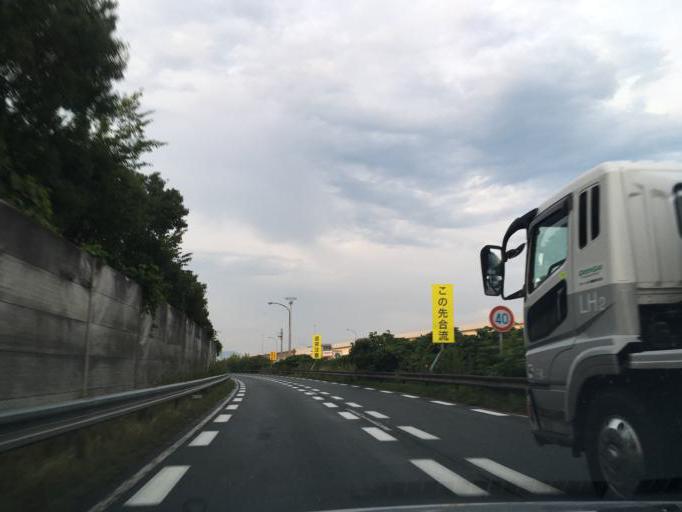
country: JP
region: Saga Prefecture
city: Tosu
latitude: 33.3982
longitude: 130.5377
